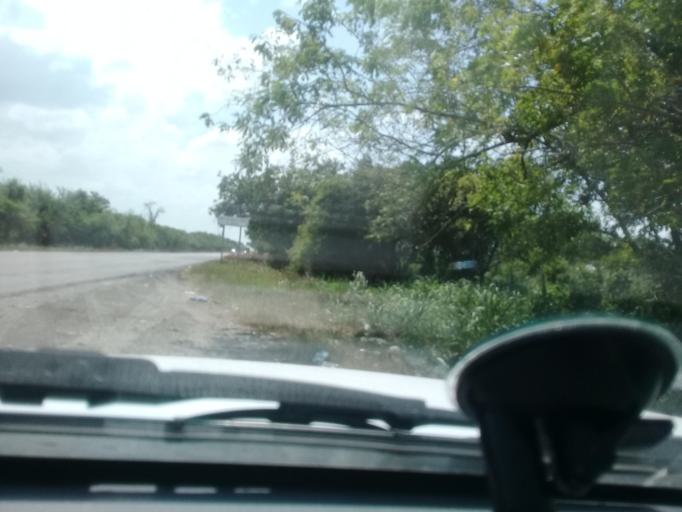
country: MX
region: Veracruz
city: Moralillo
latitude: 22.1717
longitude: -98.0528
